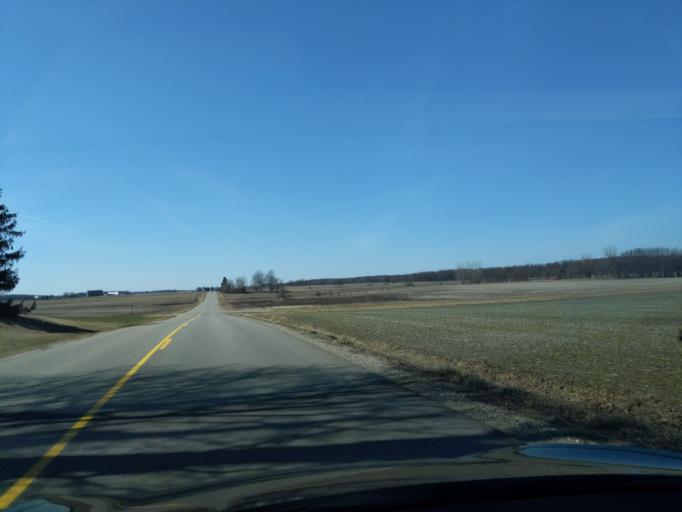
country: US
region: Michigan
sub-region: Eaton County
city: Grand Ledge
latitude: 42.7266
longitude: -84.8553
